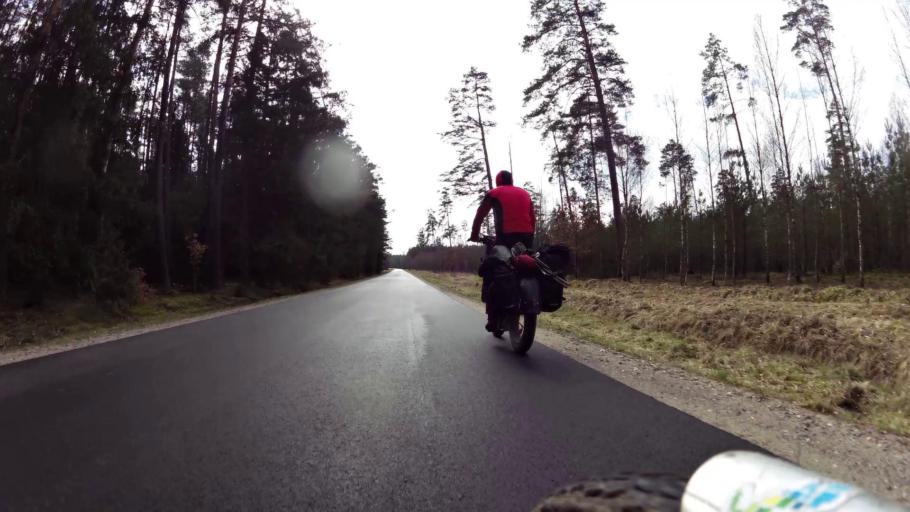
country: PL
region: Pomeranian Voivodeship
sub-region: Powiat bytowski
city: Kolczyglowy
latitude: 54.2019
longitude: 17.2352
